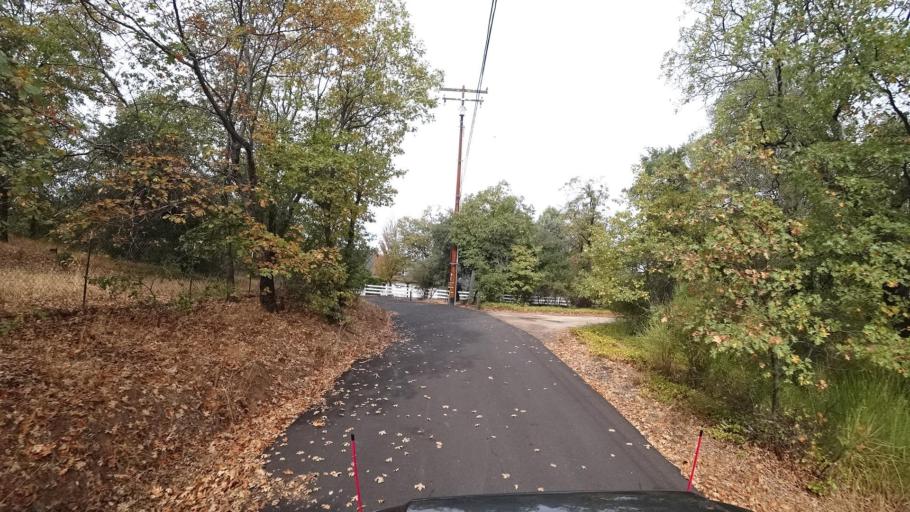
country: US
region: California
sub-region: San Diego County
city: Julian
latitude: 33.0535
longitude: -116.6237
